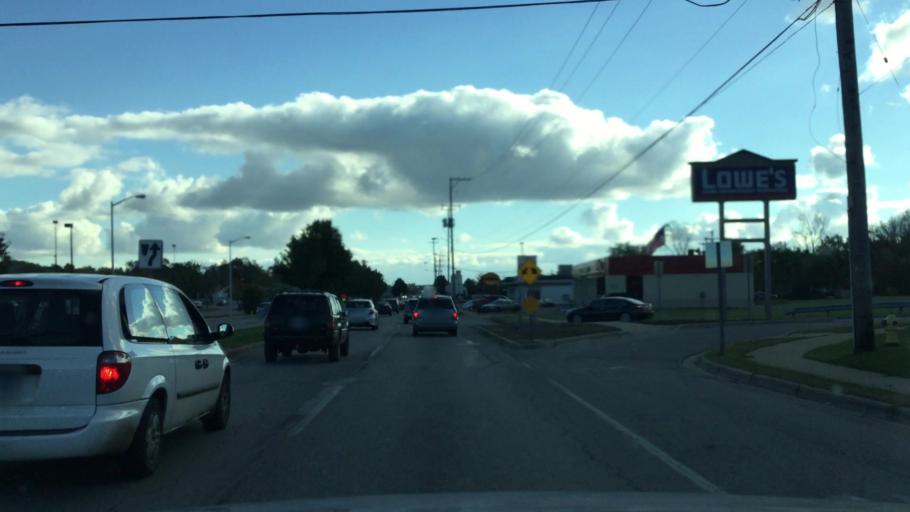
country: US
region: Michigan
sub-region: Kalamazoo County
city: Portage
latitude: 42.2440
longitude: -85.5897
